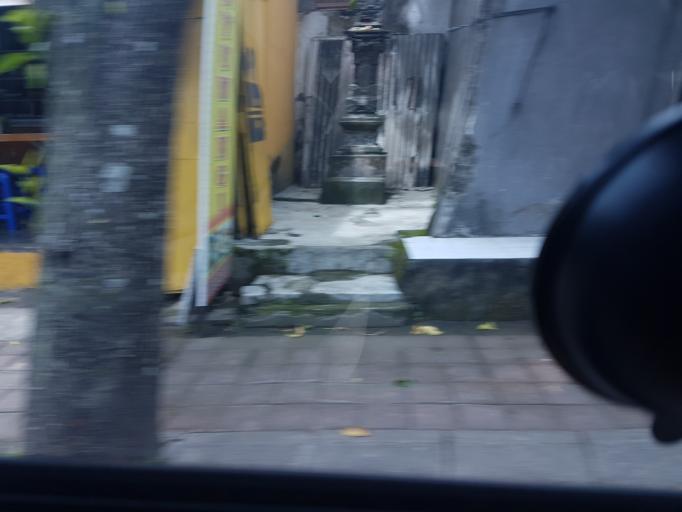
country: ID
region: Bali
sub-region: Kabupaten Gianyar
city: Ubud
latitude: -8.5382
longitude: 115.2729
